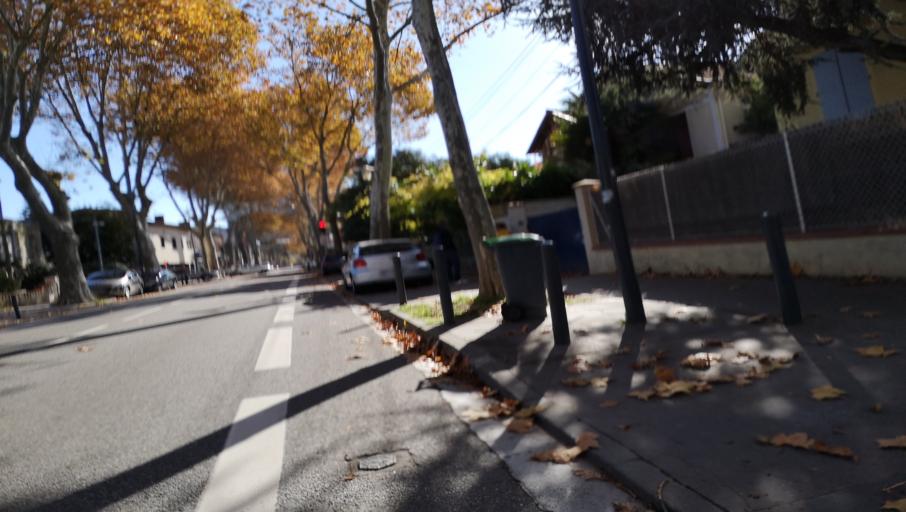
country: FR
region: Midi-Pyrenees
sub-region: Departement de la Haute-Garonne
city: Blagnac
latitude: 43.6159
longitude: 1.4094
